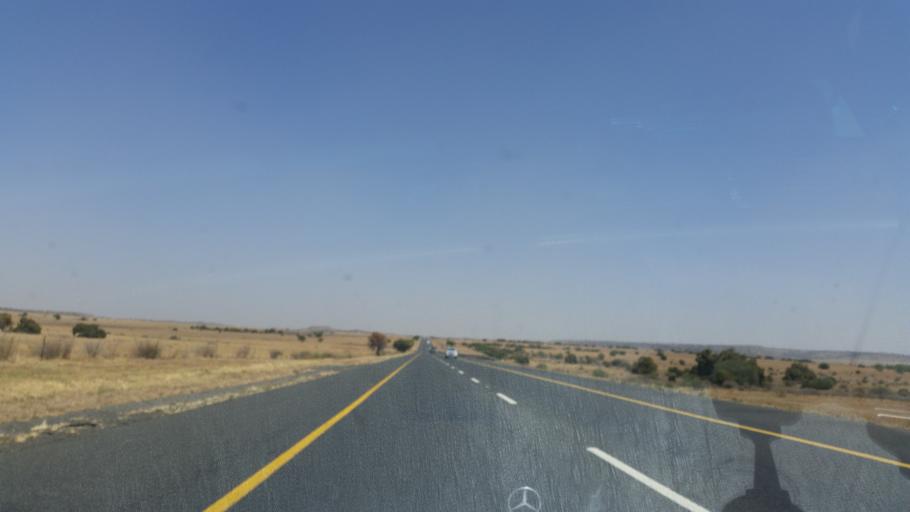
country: ZA
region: Orange Free State
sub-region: Lejweleputswa District Municipality
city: Winburg
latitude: -28.6725
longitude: 26.8425
